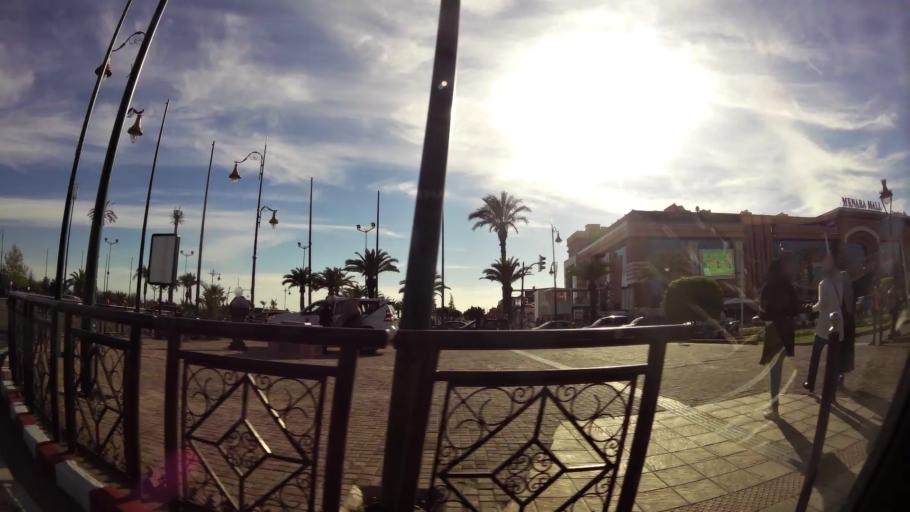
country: MA
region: Marrakech-Tensift-Al Haouz
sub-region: Marrakech
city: Marrakesh
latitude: 31.6183
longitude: -8.0082
